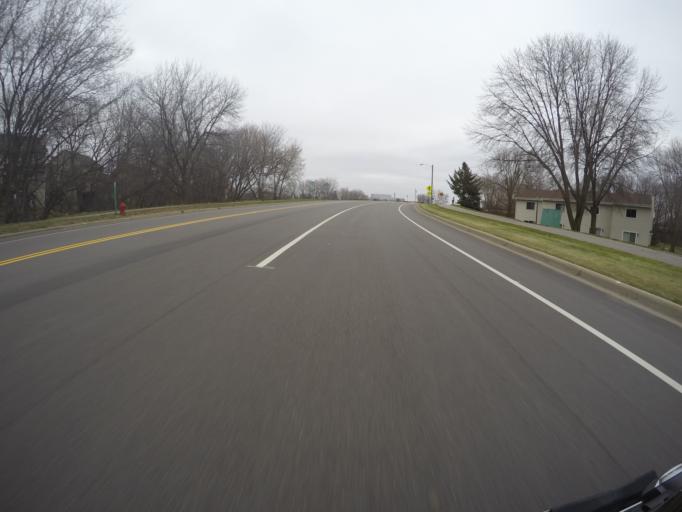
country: US
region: Minnesota
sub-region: Carver County
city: Chanhassen
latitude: 44.8734
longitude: -93.4993
